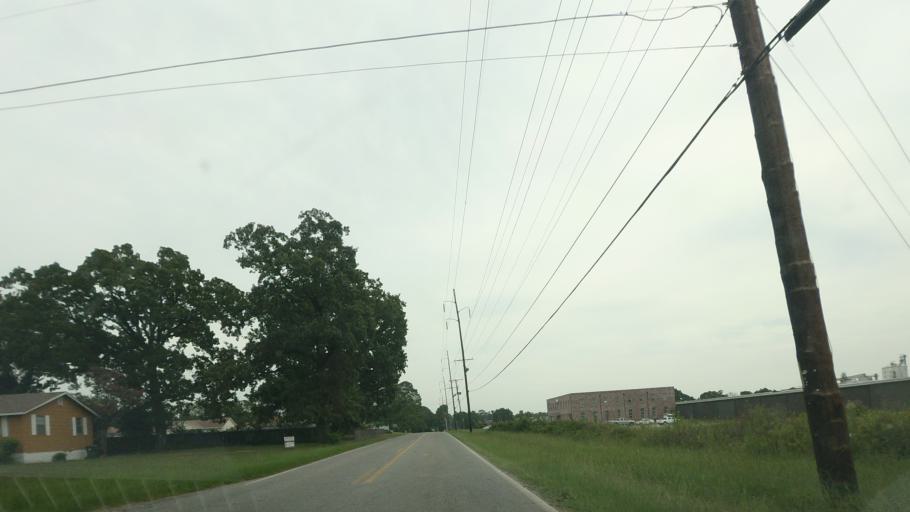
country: US
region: Georgia
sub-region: Houston County
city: Robins Air Force Base
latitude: 32.5898
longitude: -83.5984
